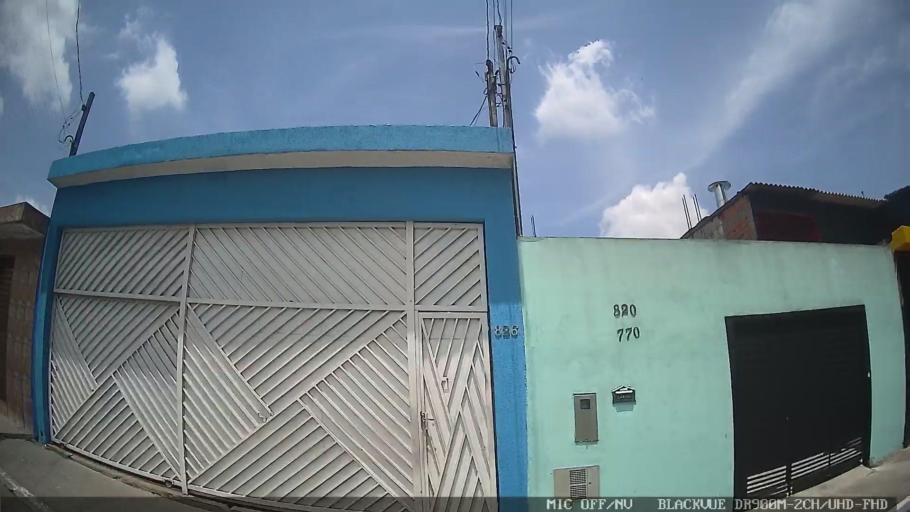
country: BR
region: Sao Paulo
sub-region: Ferraz De Vasconcelos
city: Ferraz de Vasconcelos
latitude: -23.5504
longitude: -46.4072
